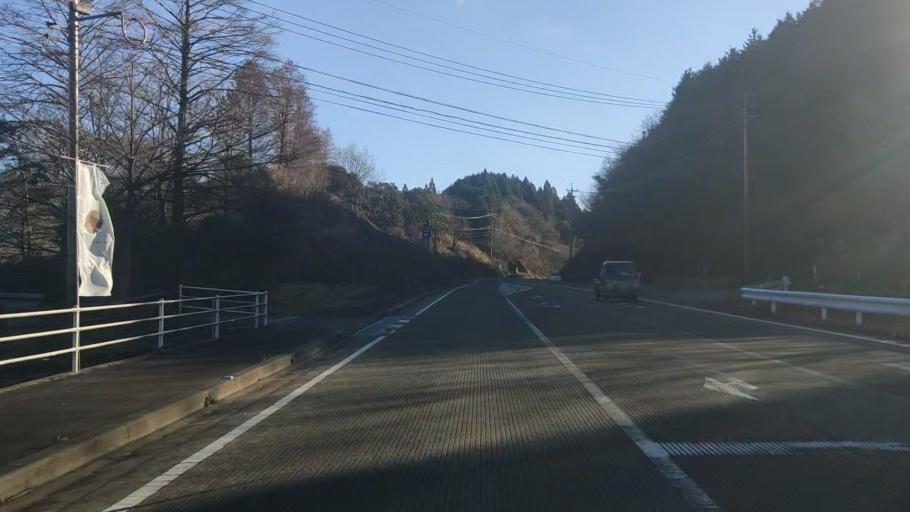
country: JP
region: Saga Prefecture
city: Kanzakimachi-kanzaki
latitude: 33.4058
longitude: 130.2725
